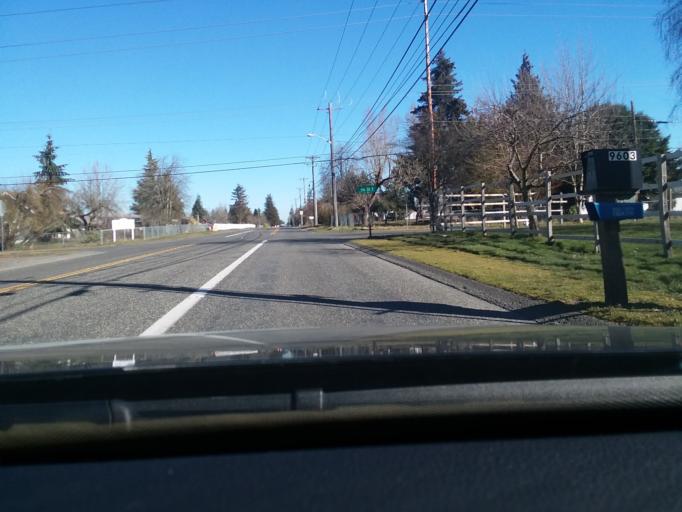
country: US
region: Washington
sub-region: Pierce County
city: Midland
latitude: 47.1696
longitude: -122.3890
